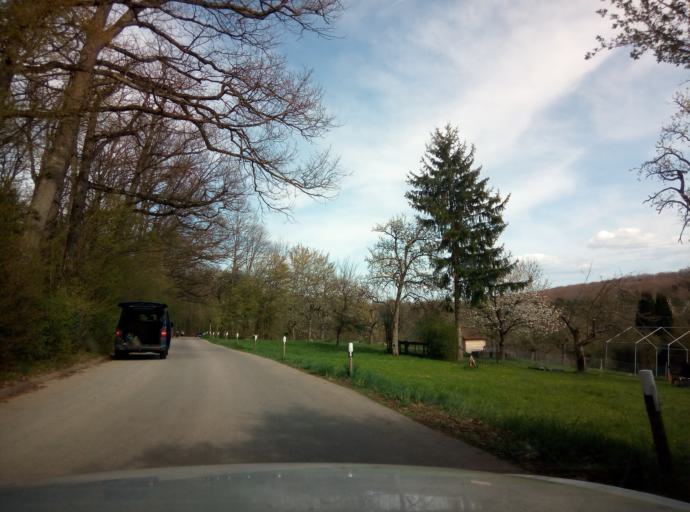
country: DE
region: Baden-Wuerttemberg
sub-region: Tuebingen Region
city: Tuebingen
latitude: 48.5038
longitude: 9.0680
